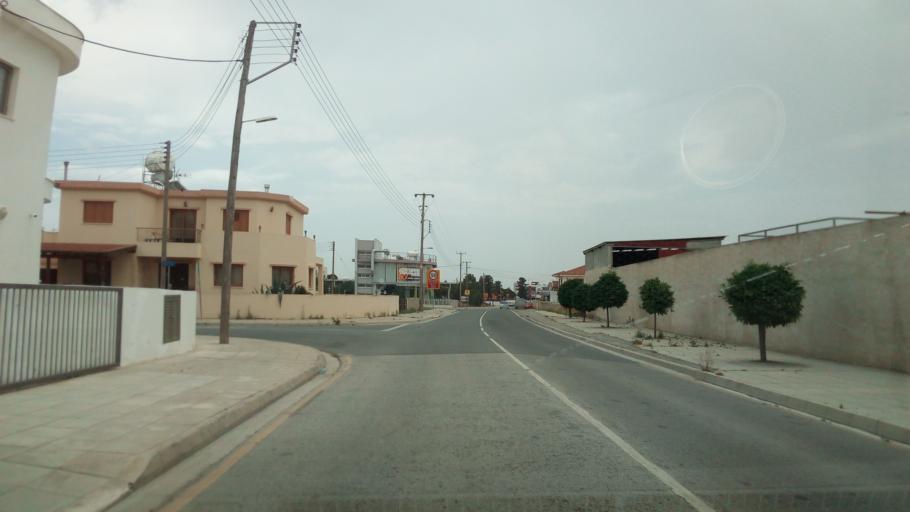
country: CY
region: Larnaka
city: Livadia
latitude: 34.9605
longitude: 33.6347
